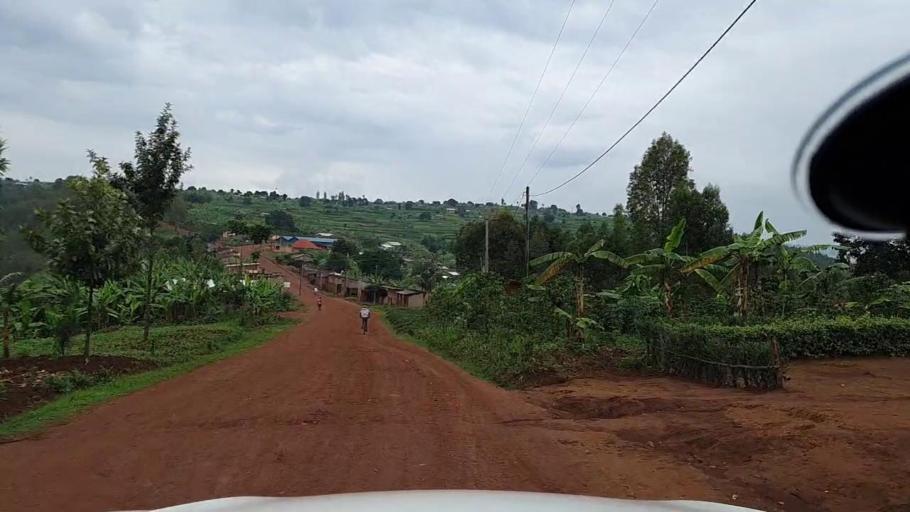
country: RW
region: Kigali
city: Kigali
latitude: -1.9067
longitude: 29.8987
